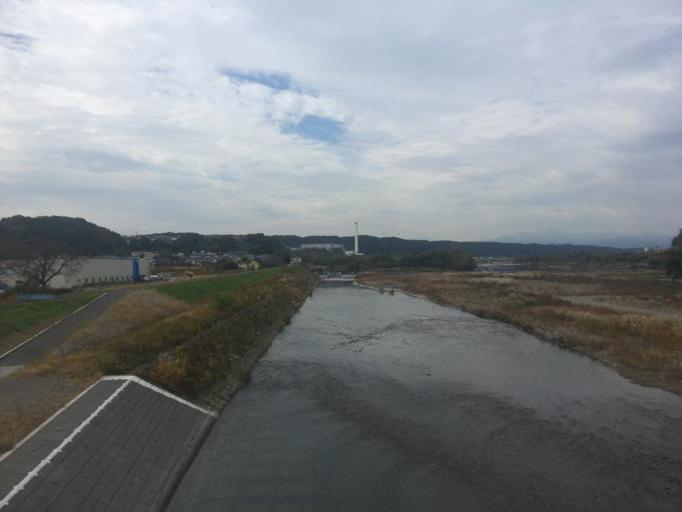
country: JP
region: Tokyo
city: Hino
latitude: 35.6932
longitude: 139.3631
